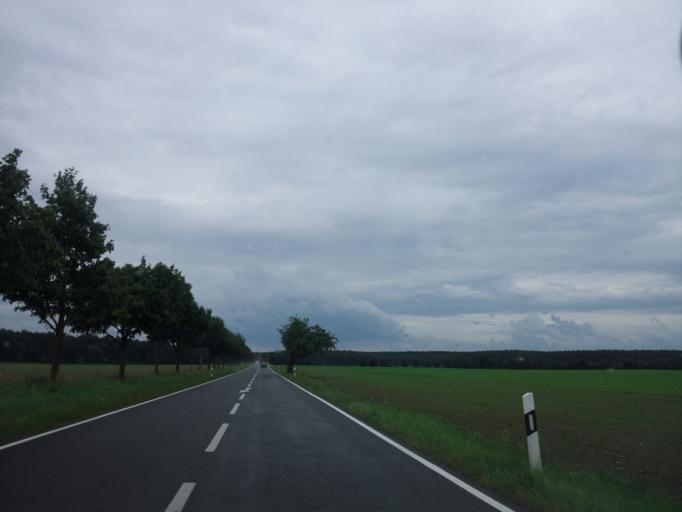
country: DE
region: Brandenburg
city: Wiesenburg
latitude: 52.1647
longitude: 12.4805
